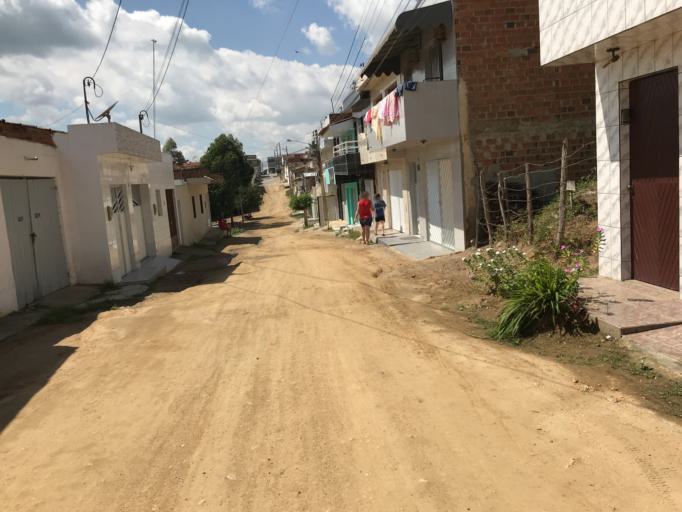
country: BR
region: Pernambuco
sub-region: Bezerros
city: Bezerros
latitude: -8.2300
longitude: -35.7560
